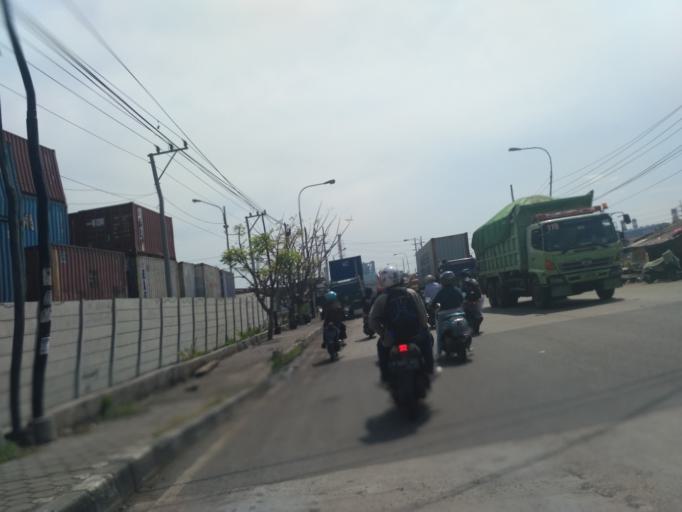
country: ID
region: Central Java
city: Semarang
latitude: -6.9586
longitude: 110.4307
